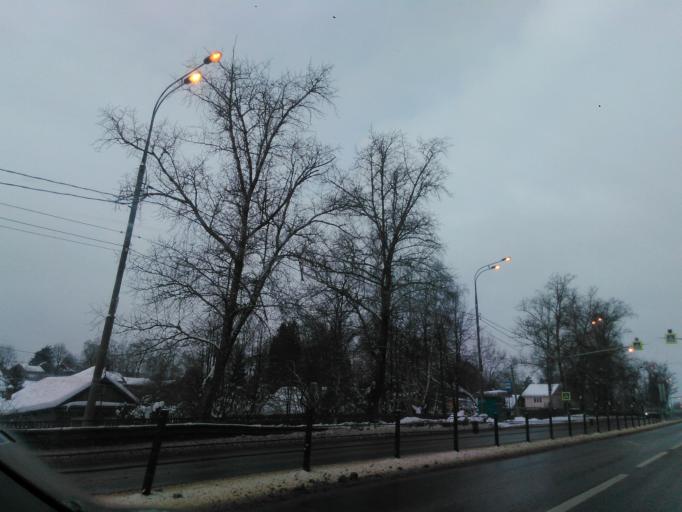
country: RU
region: Moskovskaya
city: Dedenevo
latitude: 56.2430
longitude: 37.5247
